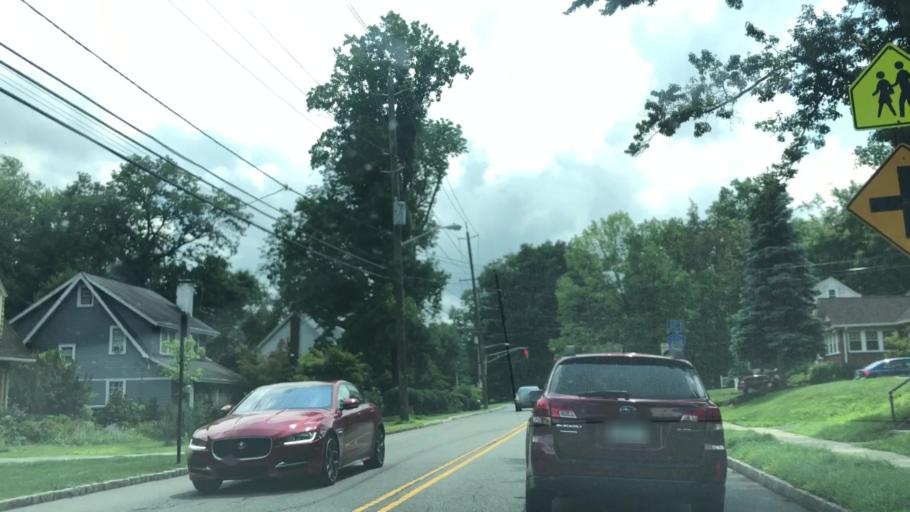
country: US
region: New Jersey
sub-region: Passaic County
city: Little Falls
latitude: 40.8592
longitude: -74.2036
